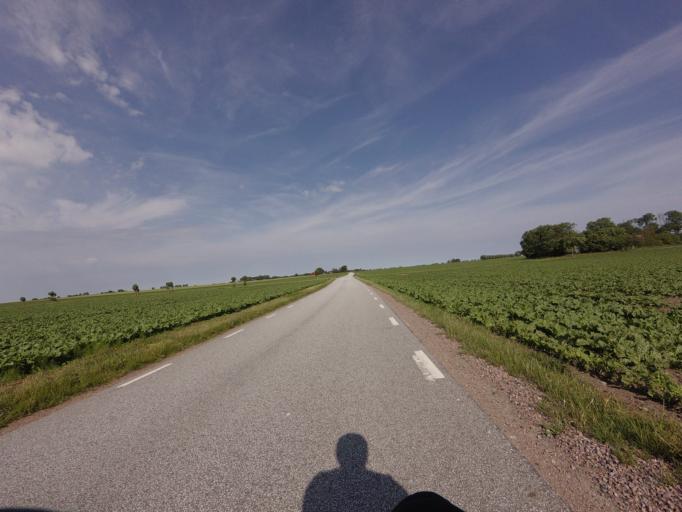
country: SE
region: Skane
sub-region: Vellinge Kommun
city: Vellinge
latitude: 55.4981
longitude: 13.0551
